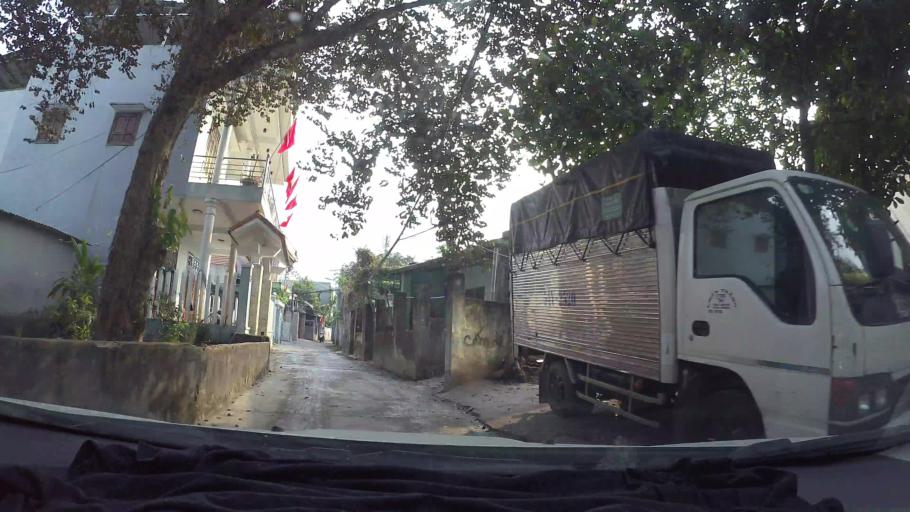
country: VN
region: Da Nang
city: Lien Chieu
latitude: 16.0510
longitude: 108.1539
